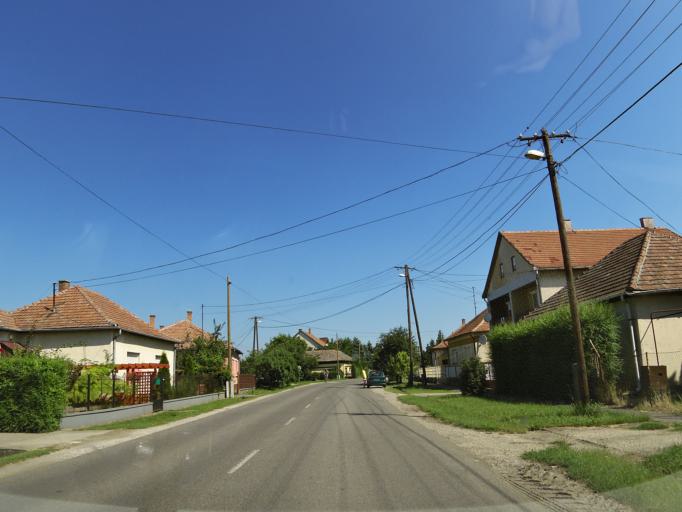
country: HU
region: Jasz-Nagykun-Szolnok
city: Toszeg
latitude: 47.0981
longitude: 20.1488
